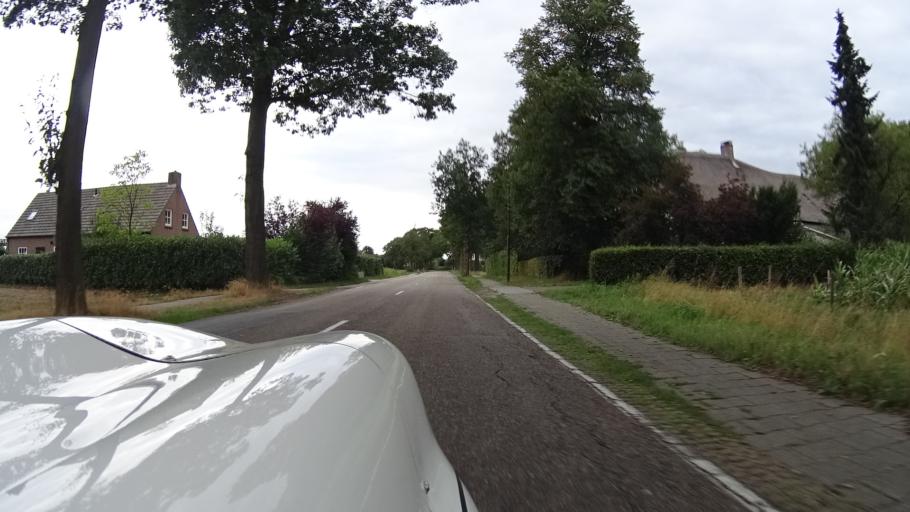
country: NL
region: North Brabant
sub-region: Gemeente Sint-Michielsgestel
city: Sint-Michielsgestel
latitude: 51.6966
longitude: 5.4000
